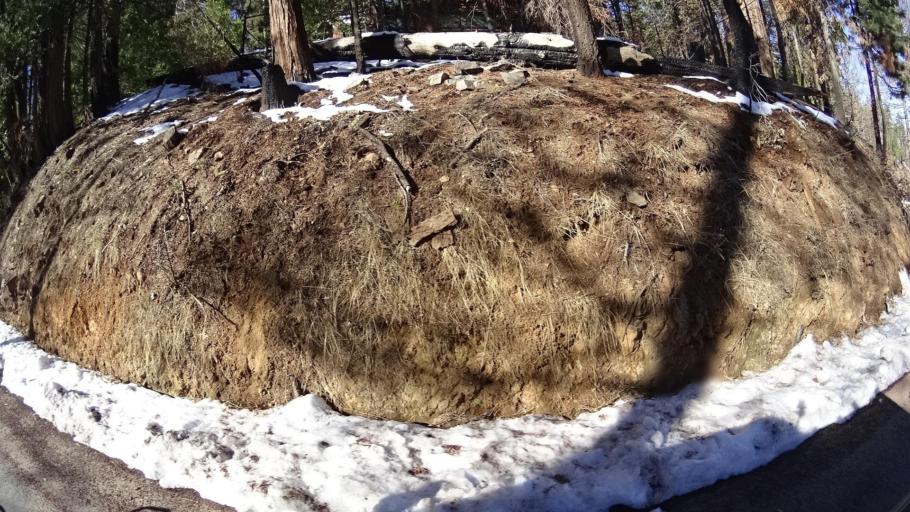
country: US
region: California
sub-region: Kern County
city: Alta Sierra
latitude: 35.7146
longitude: -118.5542
